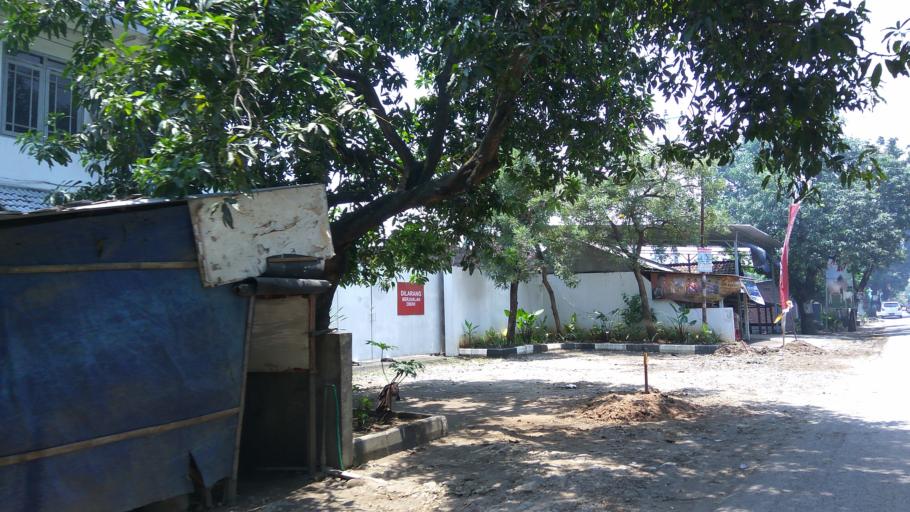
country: ID
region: Central Java
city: Mranggen
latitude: -7.0307
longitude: 110.5366
